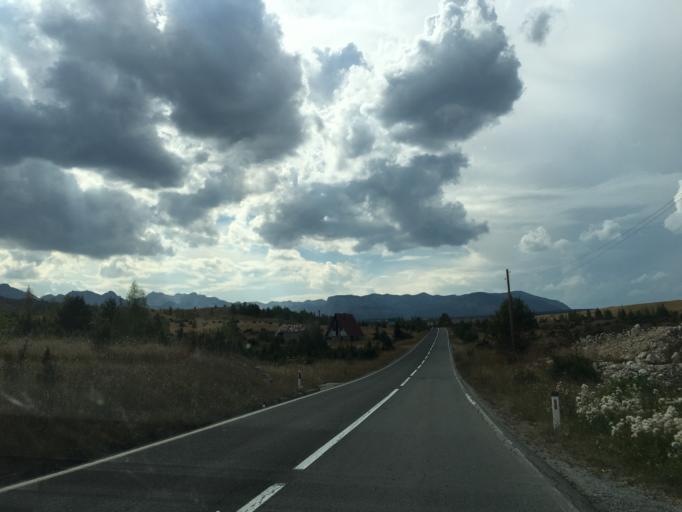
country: ME
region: Opstina Zabljak
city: Zabljak
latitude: 43.1647
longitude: 19.1742
